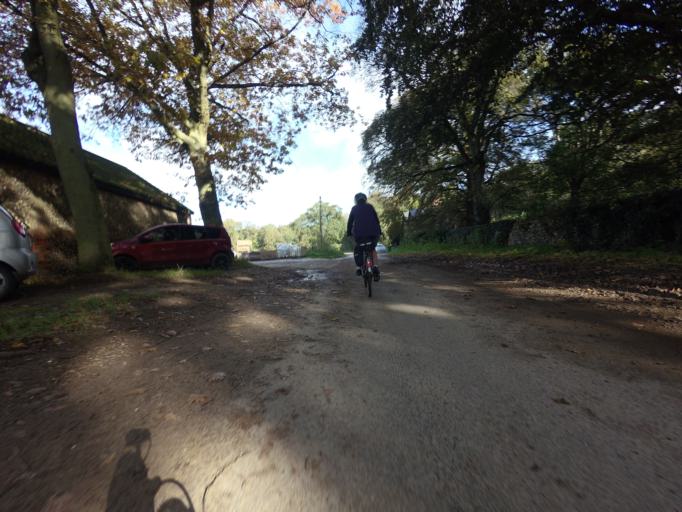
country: GB
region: England
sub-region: Norfolk
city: Dersingham
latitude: 52.8589
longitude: 0.6657
